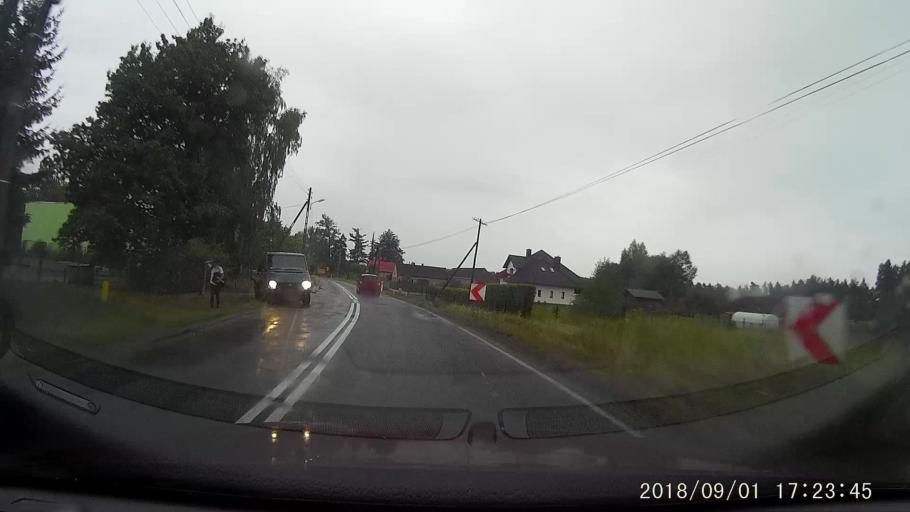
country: PL
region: Lubusz
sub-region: Powiat zaganski
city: Zagan
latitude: 51.6972
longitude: 15.2971
